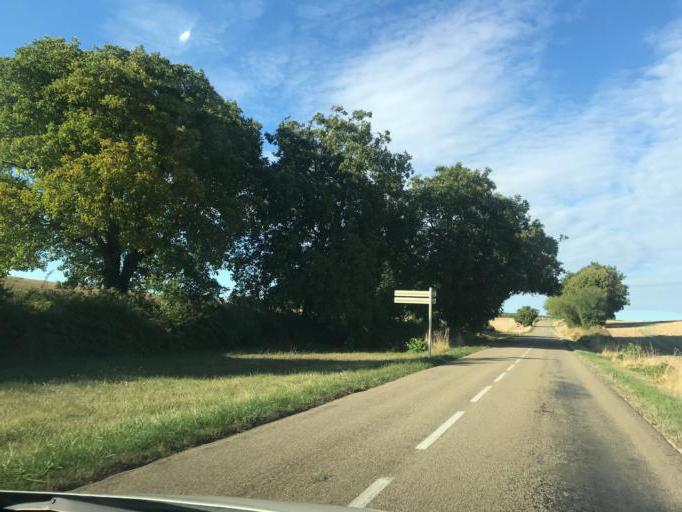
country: FR
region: Bourgogne
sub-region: Departement de l'Yonne
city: Fontenailles
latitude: 47.5550
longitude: 3.4309
